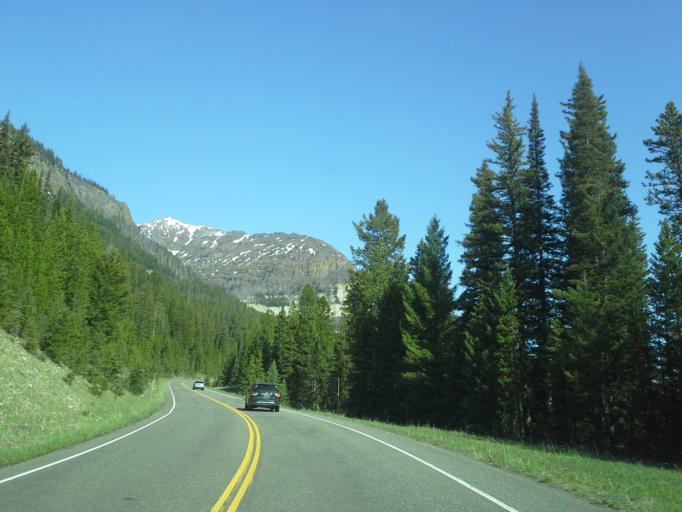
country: US
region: Montana
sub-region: Carbon County
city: Red Lodge
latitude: 44.9818
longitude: -109.8448
